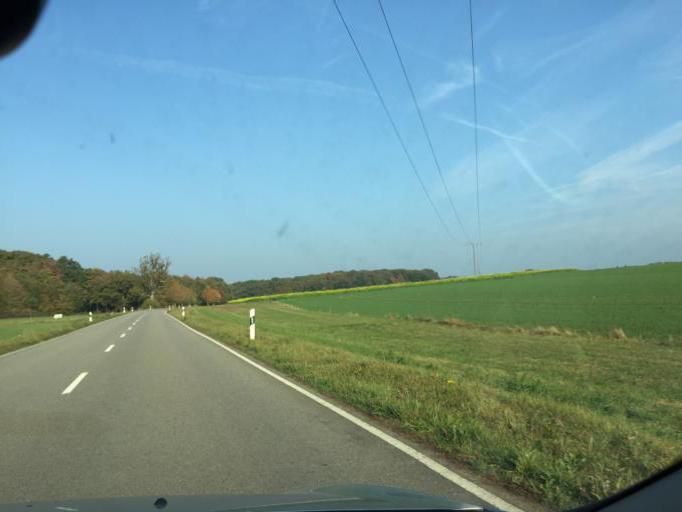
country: LU
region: Luxembourg
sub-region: Canton de Luxembourg
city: Contern
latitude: 49.5536
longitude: 6.2295
